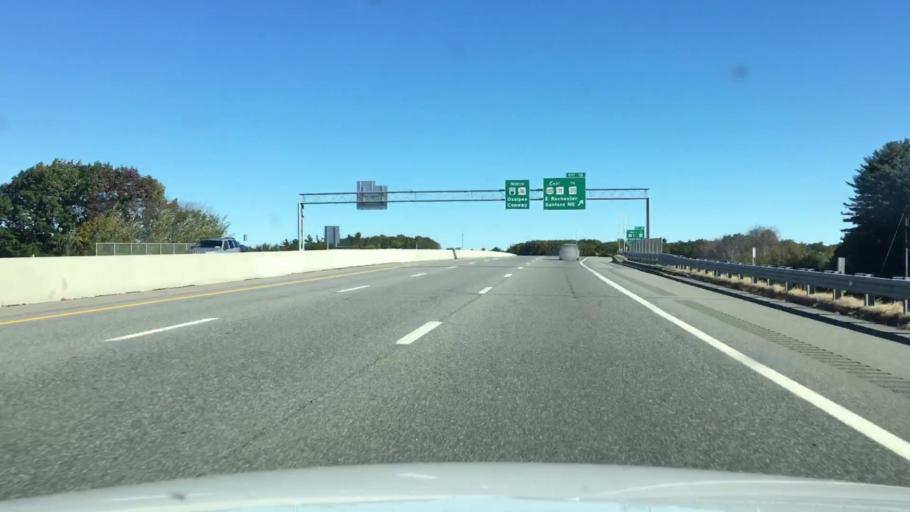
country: US
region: New Hampshire
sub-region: Strafford County
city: Rochester
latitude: 43.3237
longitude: -70.9898
